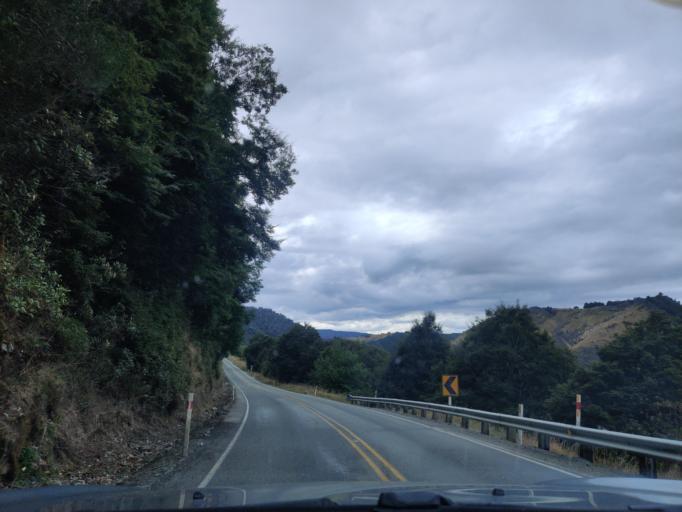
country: NZ
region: Tasman
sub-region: Tasman District
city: Wakefield
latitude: -41.7050
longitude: 172.6512
